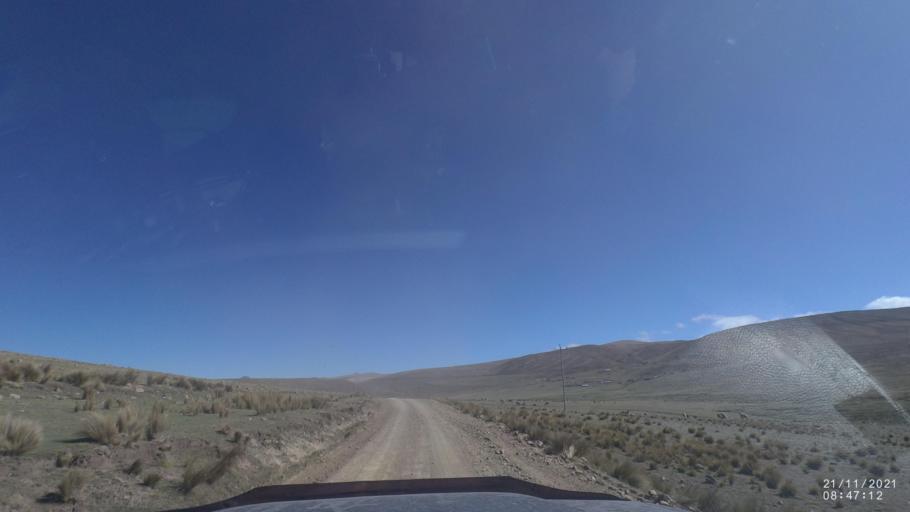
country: BO
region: Cochabamba
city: Cochabamba
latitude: -17.2377
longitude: -66.2331
